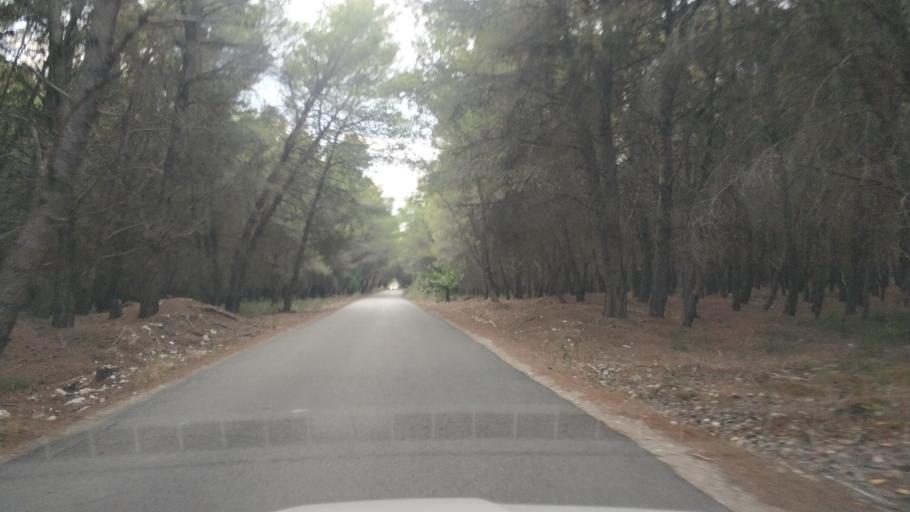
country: AL
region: Vlore
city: Vlore
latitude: 40.4967
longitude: 19.4323
